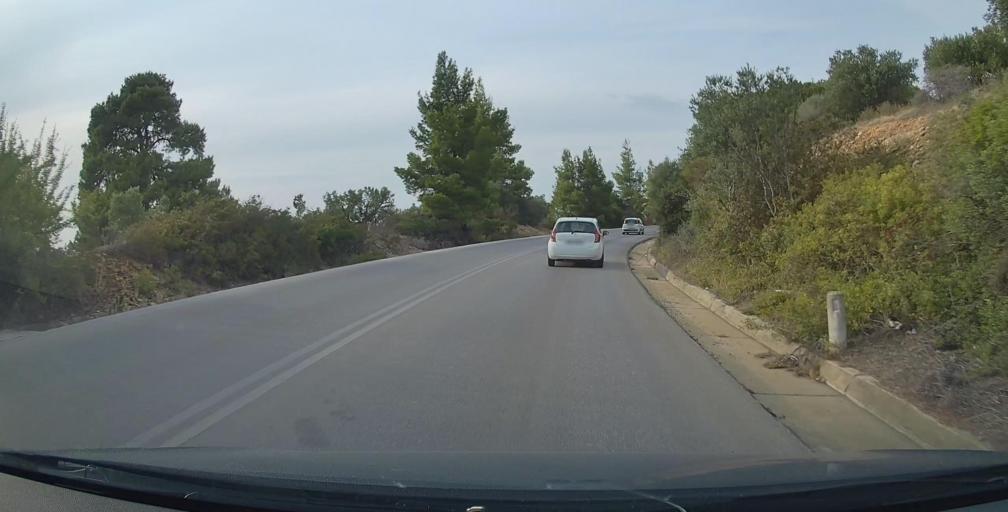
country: GR
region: Central Macedonia
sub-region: Nomos Chalkidikis
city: Neos Marmaras
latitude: 40.1552
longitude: 23.7322
